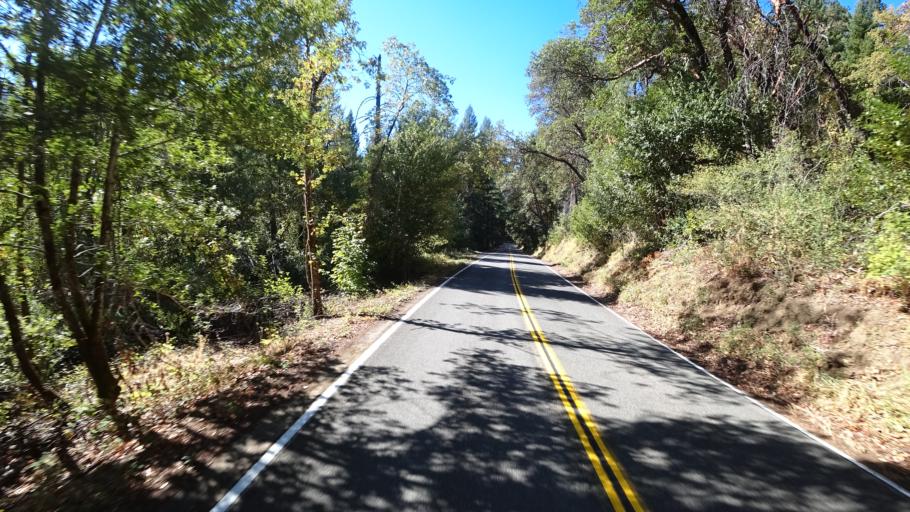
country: US
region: California
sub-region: Siskiyou County
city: Happy Camp
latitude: 41.3772
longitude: -123.4428
